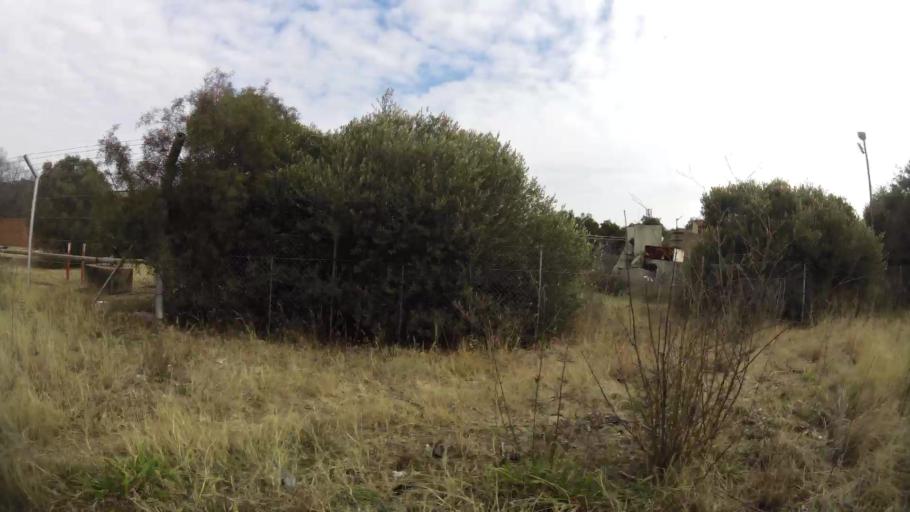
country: ZA
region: Orange Free State
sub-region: Mangaung Metropolitan Municipality
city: Bloemfontein
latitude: -29.1306
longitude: 26.2046
